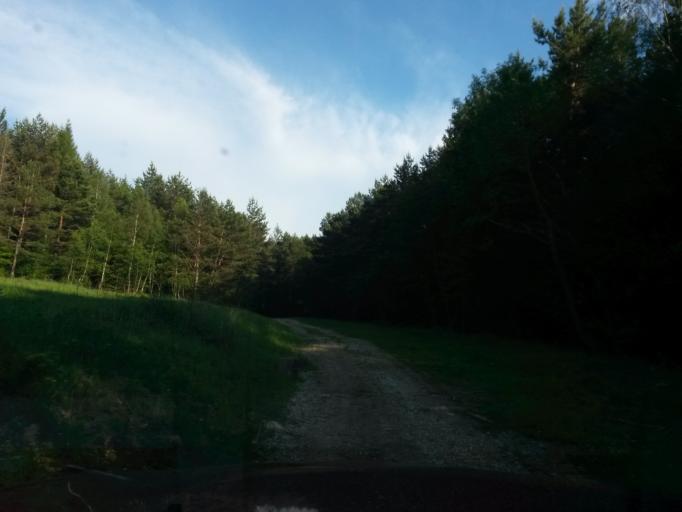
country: SK
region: Kosicky
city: Moldava nad Bodvou
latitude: 48.7431
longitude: 21.0280
